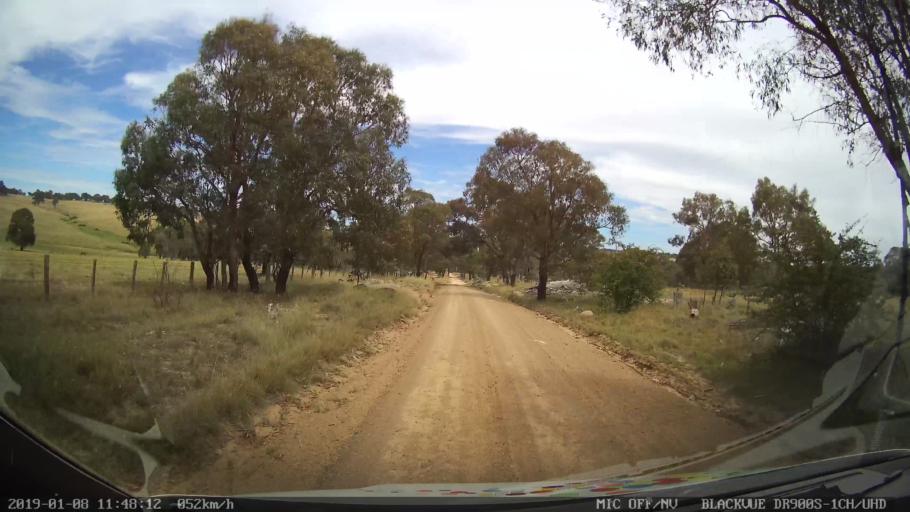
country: AU
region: New South Wales
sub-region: Armidale Dumaresq
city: Armidale
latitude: -30.3765
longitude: 151.5669
